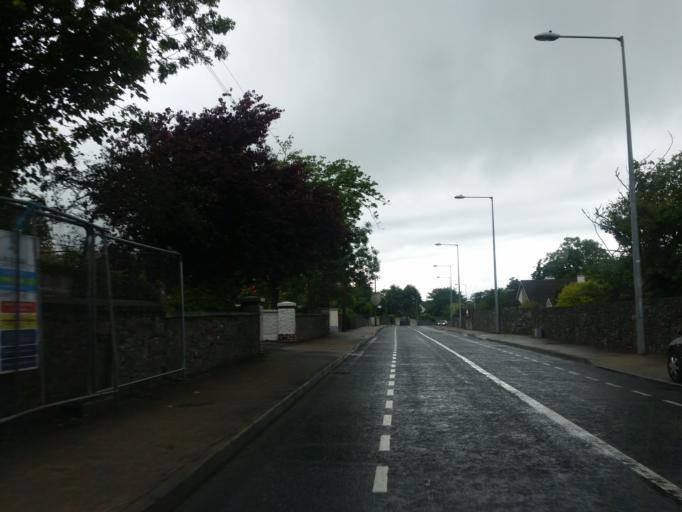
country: IE
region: Connaught
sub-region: Sligo
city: Sligo
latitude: 54.2717
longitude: -8.5075
